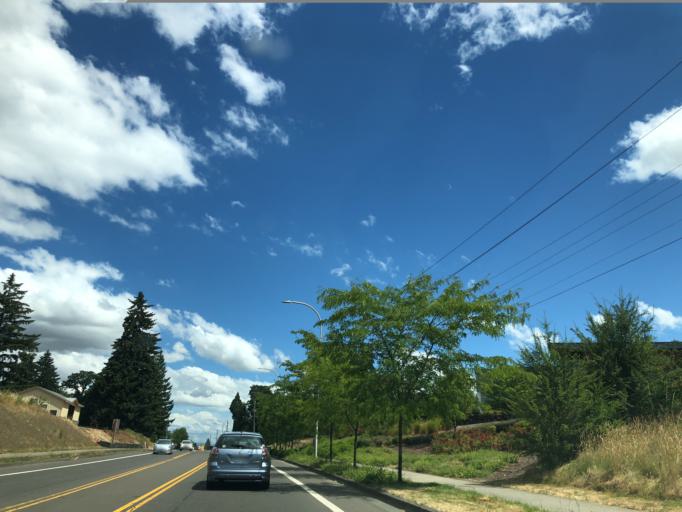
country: US
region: Oregon
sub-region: Marion County
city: Woodburn
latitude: 45.1517
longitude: -122.8440
